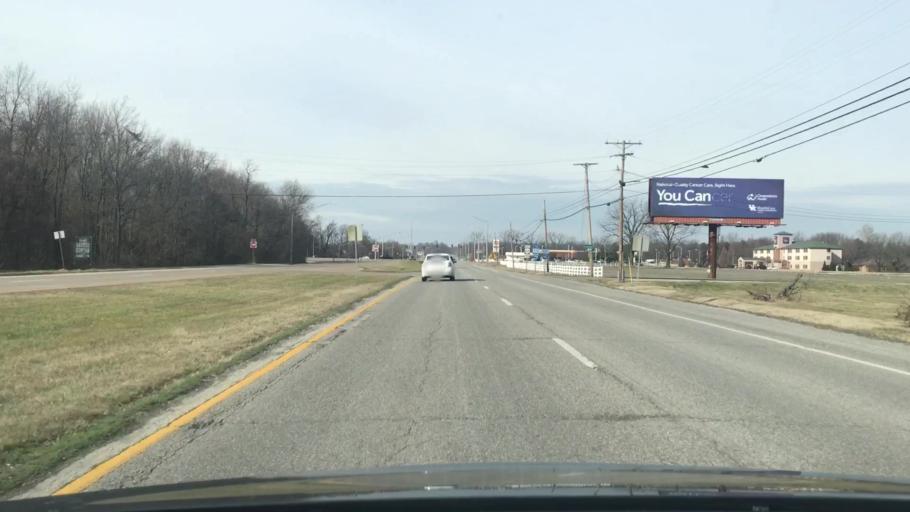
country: US
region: Kentucky
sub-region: Daviess County
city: Owensboro
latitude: 37.7741
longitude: -87.1615
